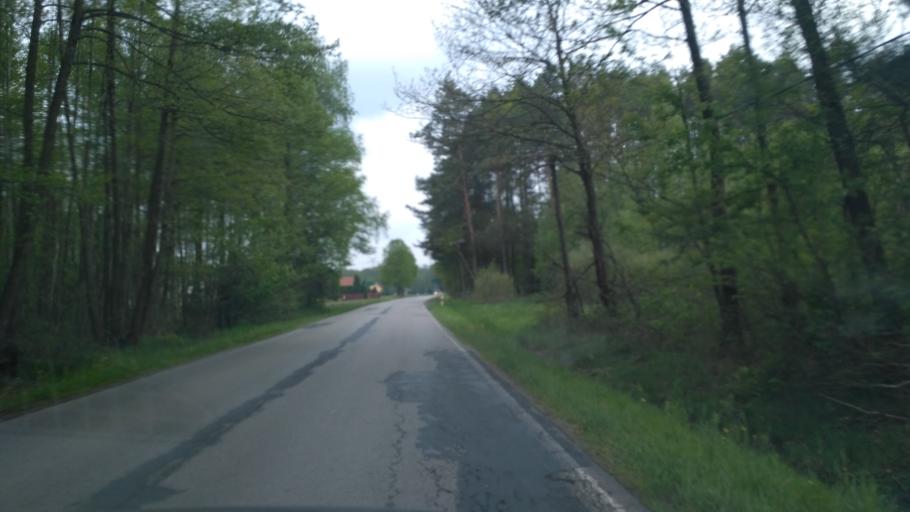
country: PL
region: Subcarpathian Voivodeship
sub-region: Powiat kolbuszowski
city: Kolbuszowa
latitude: 50.1929
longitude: 21.7679
